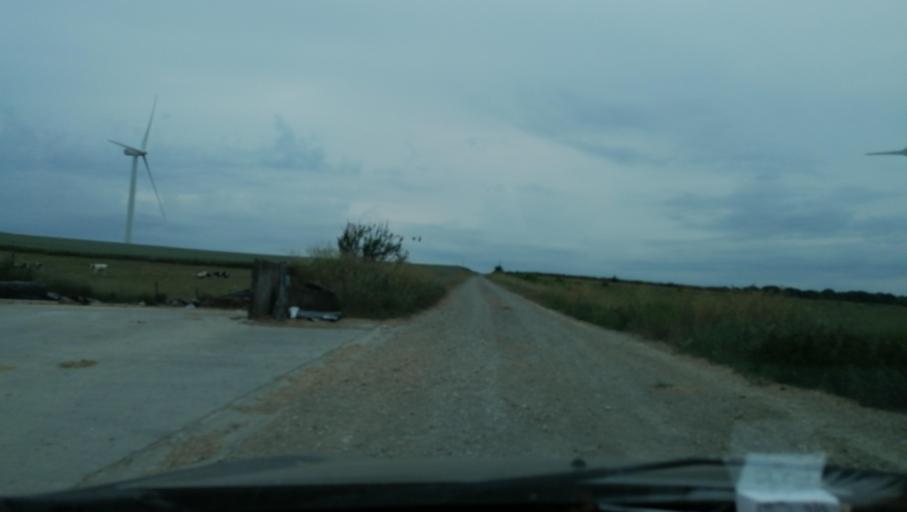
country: BE
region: Wallonia
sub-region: Province du Hainaut
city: Beaumont
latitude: 50.2085
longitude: 4.1713
